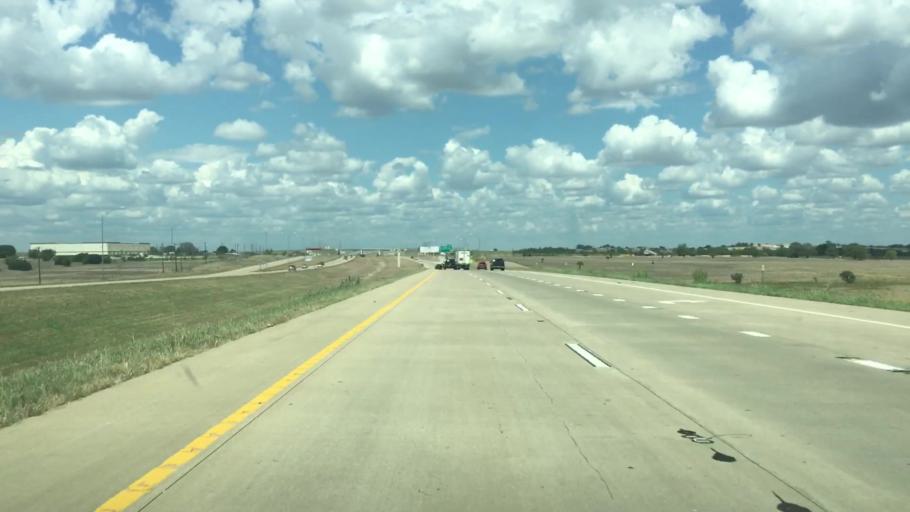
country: US
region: Texas
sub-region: Williamson County
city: Hutto
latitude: 30.5774
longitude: -97.5851
